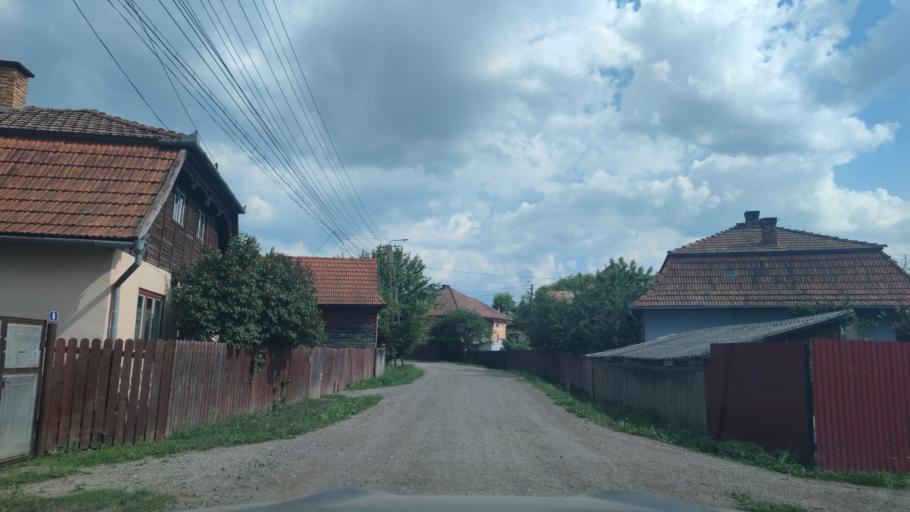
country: RO
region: Harghita
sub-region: Comuna Remetea
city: Remetea
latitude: 46.7938
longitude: 25.4459
